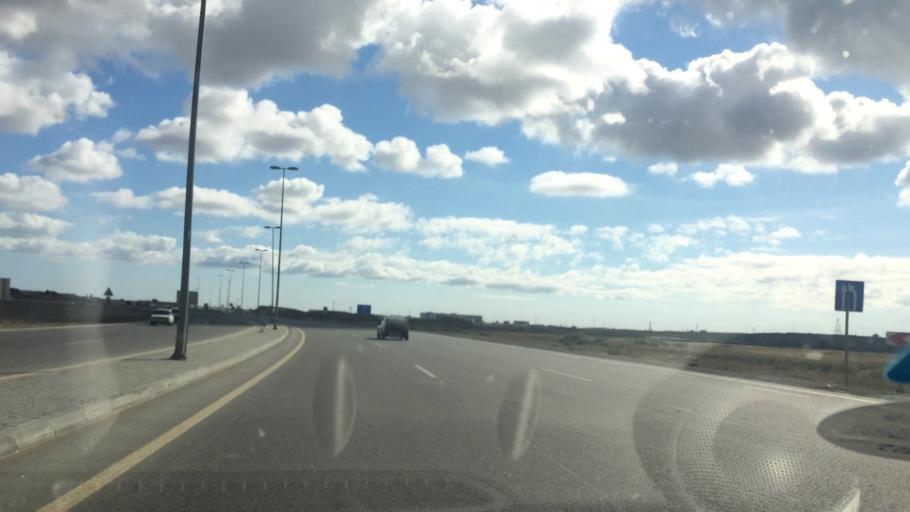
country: AZ
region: Baki
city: Mardakyany
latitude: 40.4589
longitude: 50.1285
